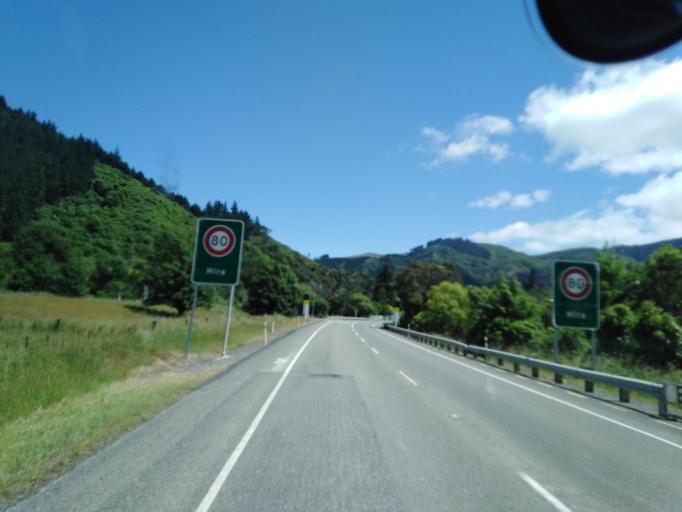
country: NZ
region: Nelson
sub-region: Nelson City
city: Nelson
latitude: -41.2184
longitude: 173.3968
